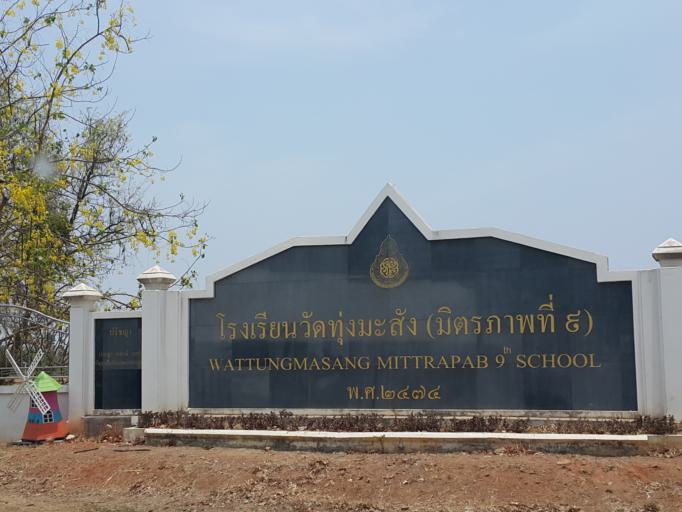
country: TH
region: Kanchanaburi
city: Bo Phloi
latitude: 14.1914
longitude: 99.4794
